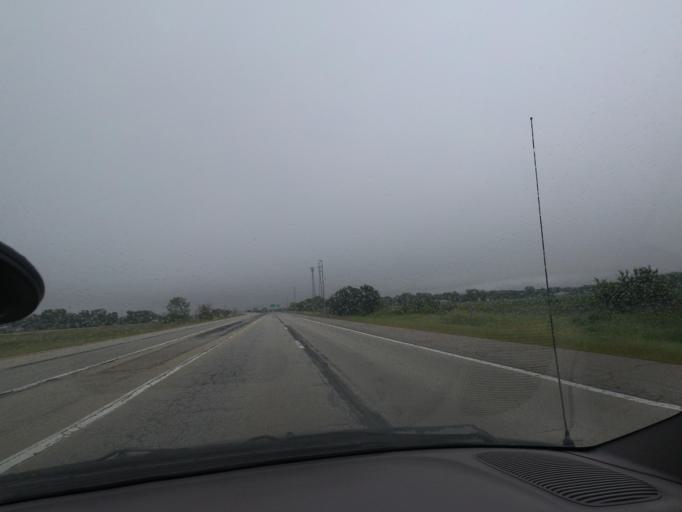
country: US
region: Illinois
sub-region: Macon County
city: Harristown
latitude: 39.8360
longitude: -89.0572
